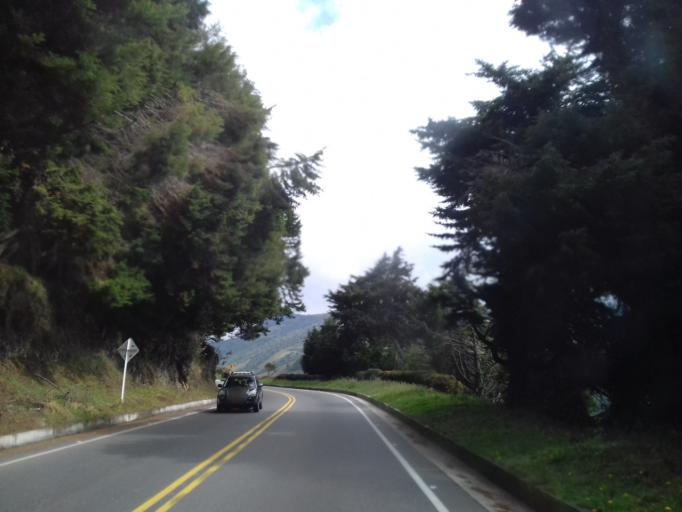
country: CO
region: Caldas
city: Villamaria
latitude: 5.0143
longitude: -75.3545
